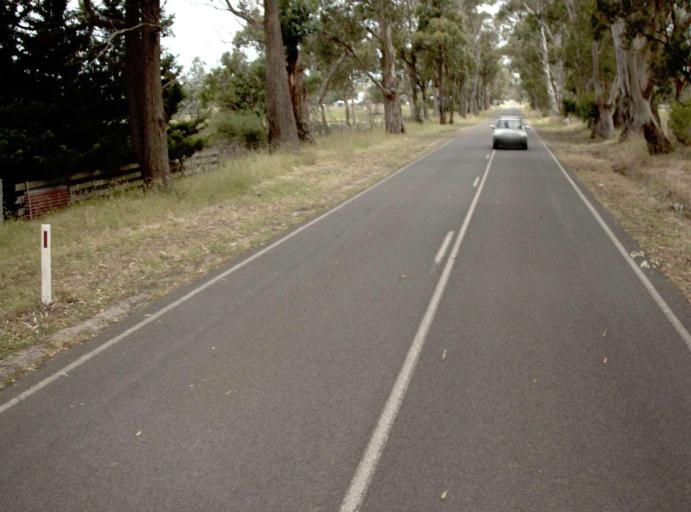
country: AU
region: Victoria
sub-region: Latrobe
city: Traralgon
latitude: -38.5115
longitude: 146.6492
